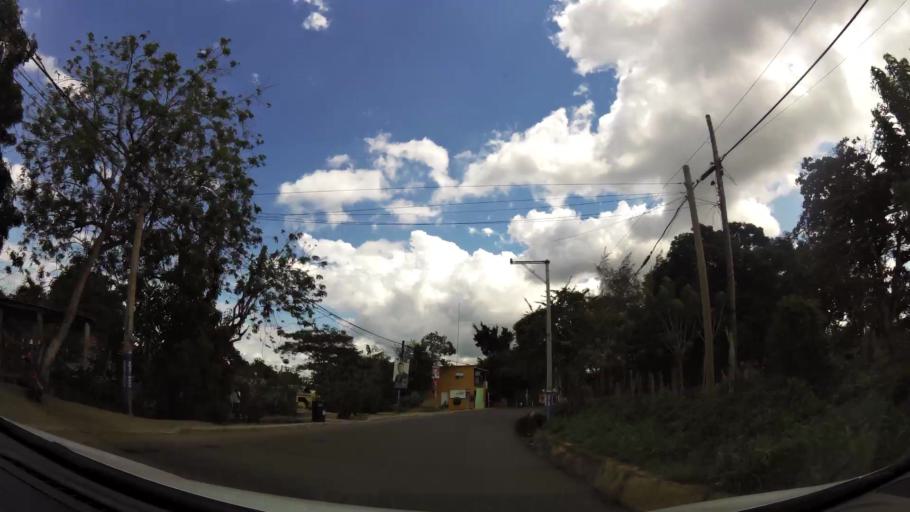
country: DO
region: Santiago
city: Licey al Medio
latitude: 19.3934
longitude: -70.6434
